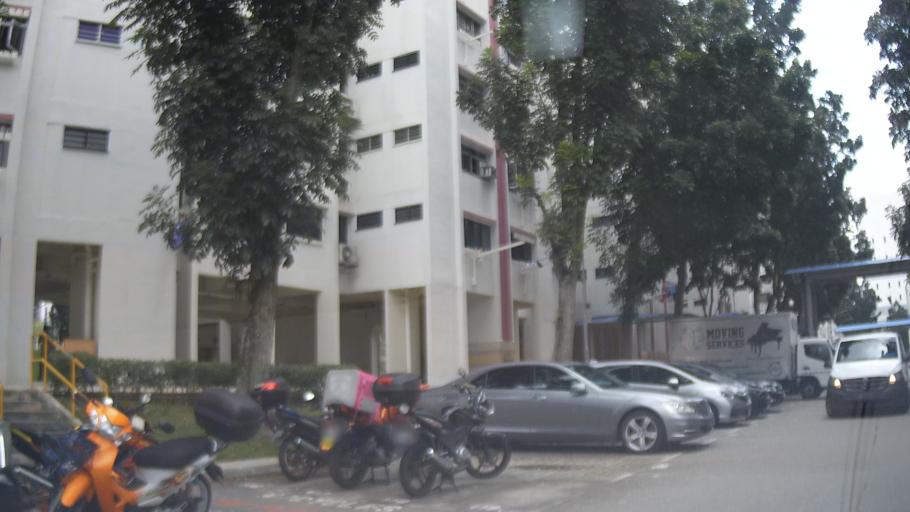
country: MY
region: Johor
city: Johor Bahru
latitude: 1.4338
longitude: 103.7760
